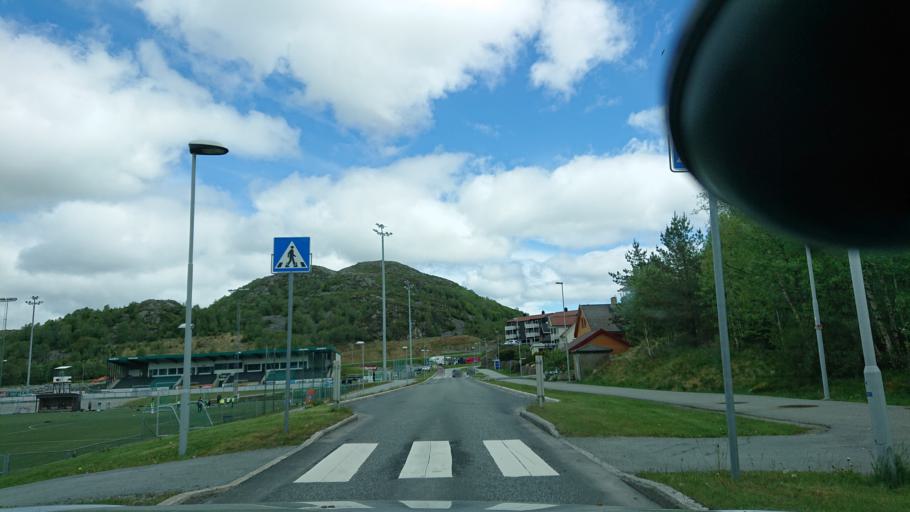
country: NO
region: Rogaland
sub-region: Gjesdal
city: Algard
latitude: 58.7737
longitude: 5.8666
